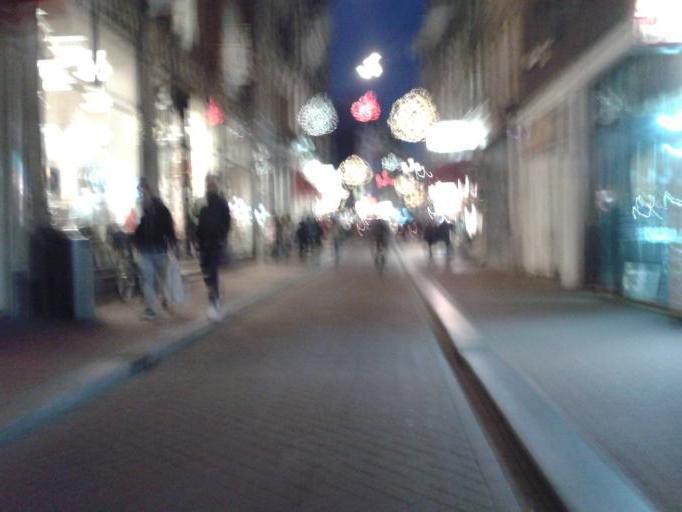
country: NL
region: North Holland
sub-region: Gemeente Amsterdam
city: Amsterdam
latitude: 52.3714
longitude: 4.8979
